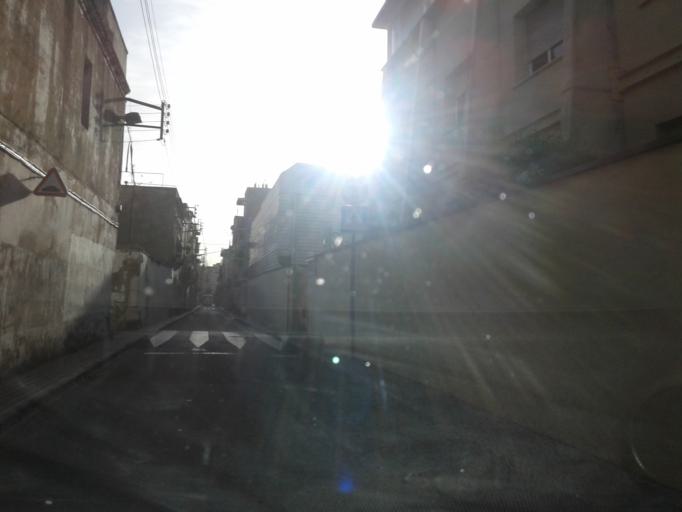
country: ES
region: Catalonia
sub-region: Provincia de Barcelona
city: Vilanova i la Geltru
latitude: 41.2284
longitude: 1.7225
